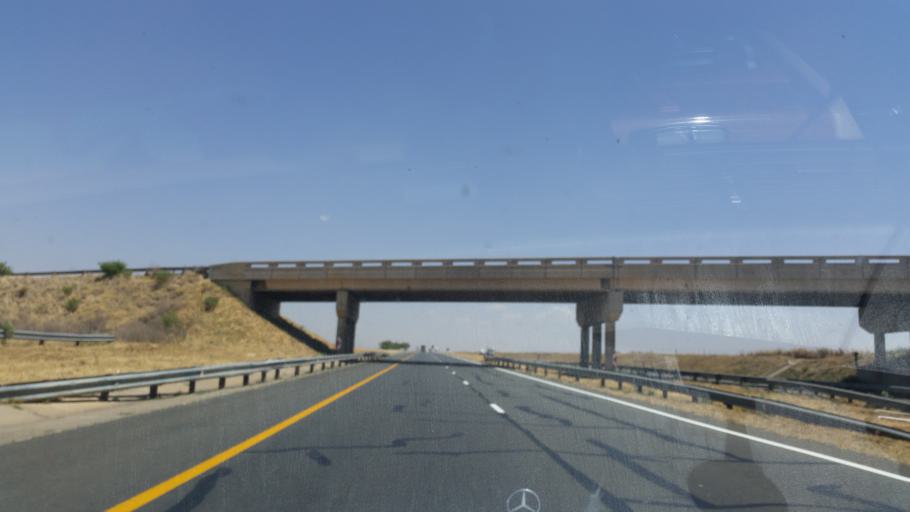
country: ZA
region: Orange Free State
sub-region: Lejweleputswa District Municipality
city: Brandfort
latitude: -28.8666
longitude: 26.5319
